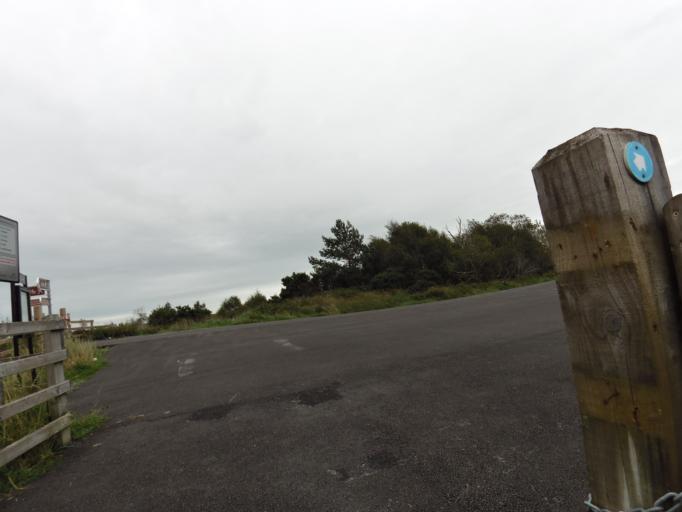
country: IE
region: Leinster
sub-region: Uibh Fhaili
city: Ferbane
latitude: 53.2549
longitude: -7.7428
